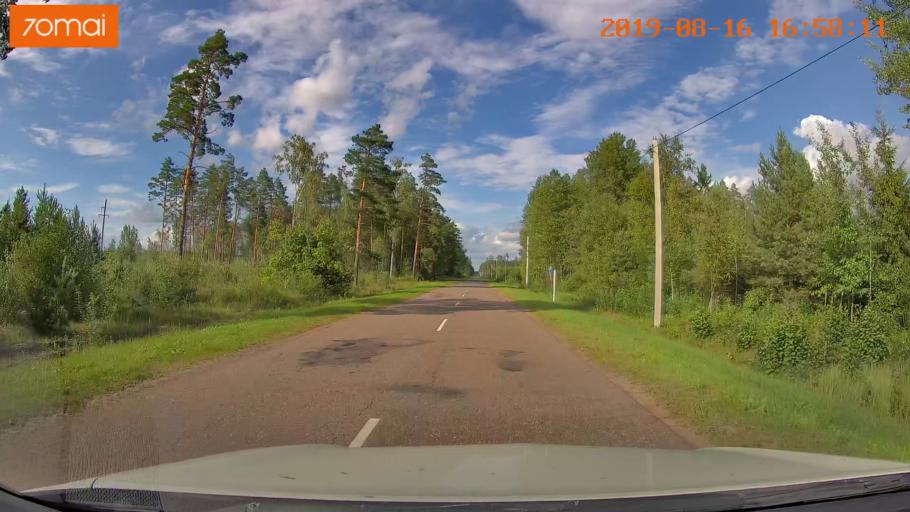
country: BY
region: Mogilev
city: Hlusha
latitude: 53.2660
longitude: 28.8311
